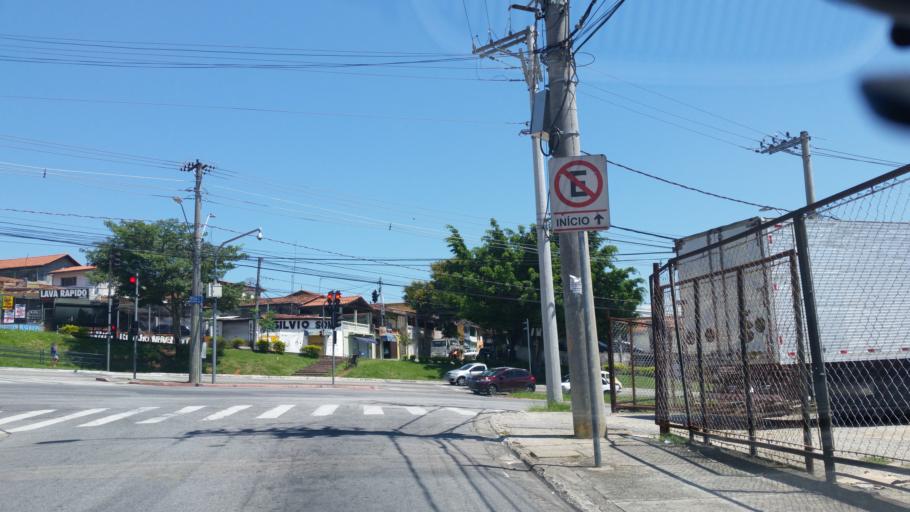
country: BR
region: Sao Paulo
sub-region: Sao Jose Dos Campos
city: Sao Jose dos Campos
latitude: -23.1709
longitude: -45.8113
